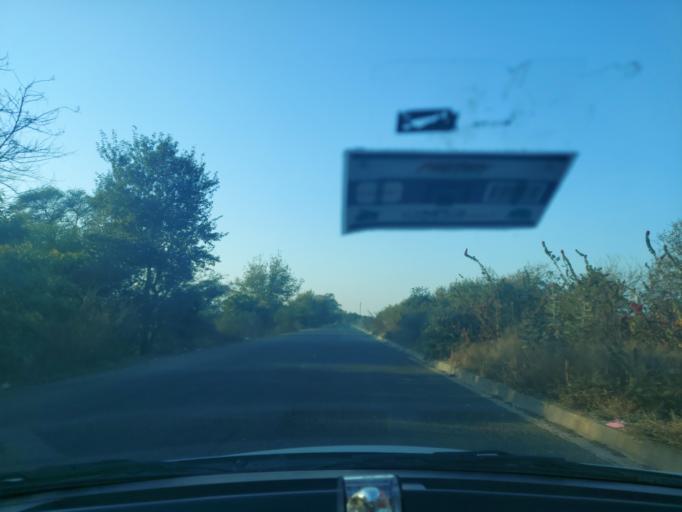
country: IN
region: Madhya Pradesh
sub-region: Indore
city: Sanwer
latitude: 23.0745
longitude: 75.8208
